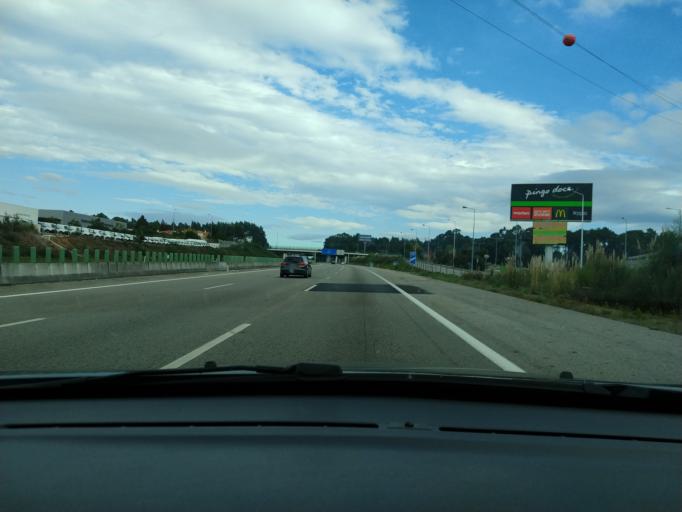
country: PT
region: Aveiro
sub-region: Santa Maria da Feira
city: Feira
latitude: 40.9205
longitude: -8.5675
